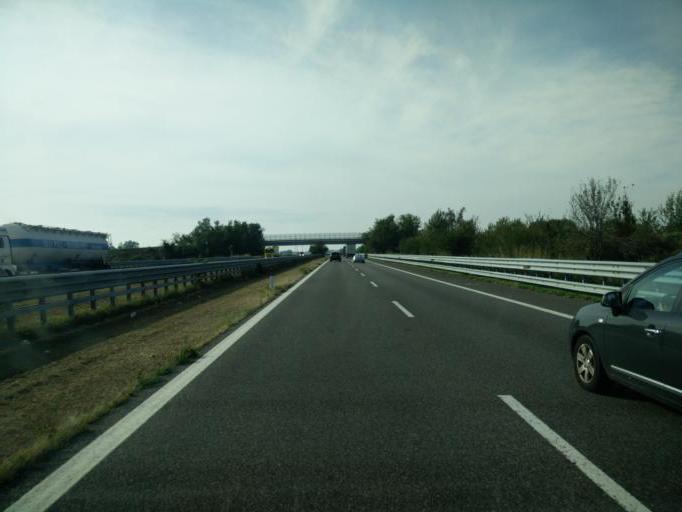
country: IT
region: Lombardy
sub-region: Provincia di Cremona
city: San Felice
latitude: 45.1661
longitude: 10.0814
